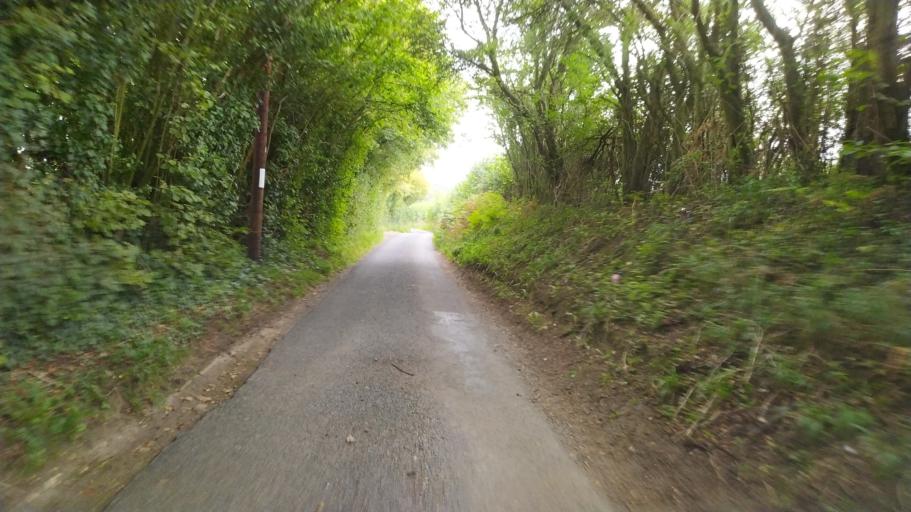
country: GB
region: England
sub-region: Hampshire
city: Long Sutton
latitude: 51.2030
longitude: -0.8944
